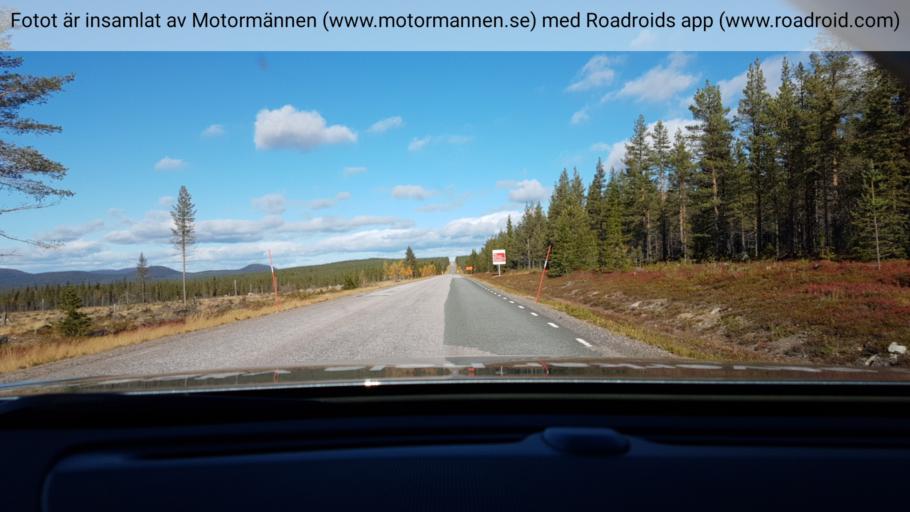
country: SE
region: Norrbotten
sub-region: Arjeplogs Kommun
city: Arjeplog
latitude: 65.8159
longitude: 18.4454
